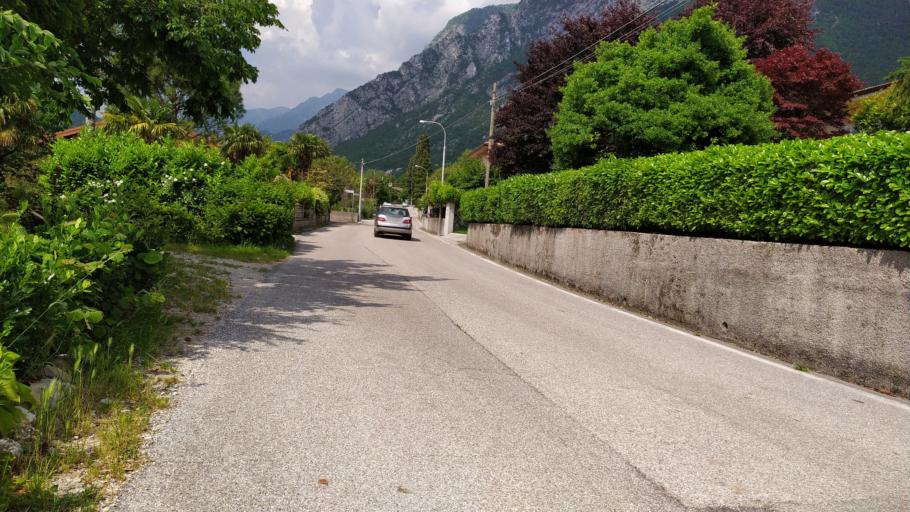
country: IT
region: Friuli Venezia Giulia
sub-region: Provincia di Udine
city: Gemona
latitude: 46.2877
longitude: 13.1381
